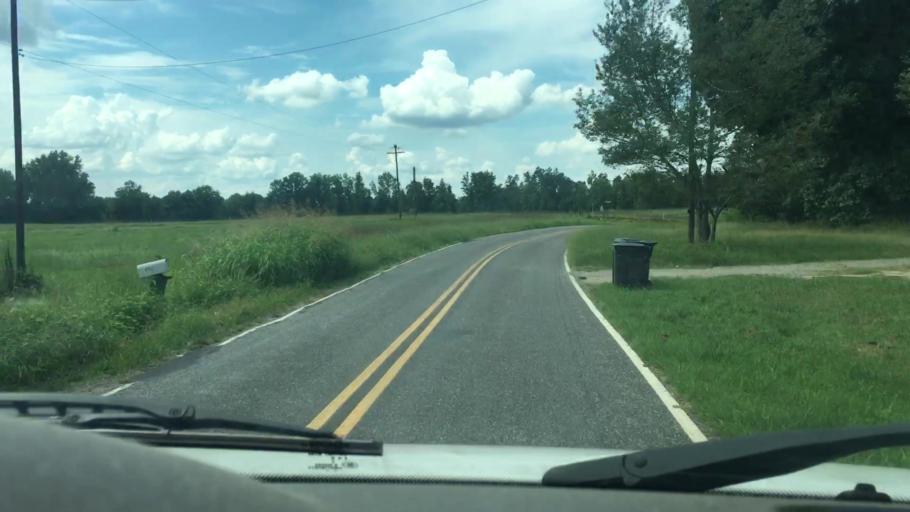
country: US
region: North Carolina
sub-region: Iredell County
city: Troutman
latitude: 35.6721
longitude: -80.8396
